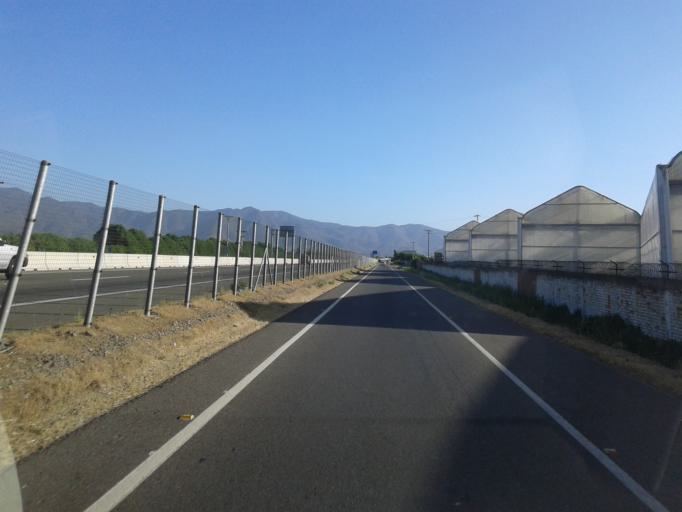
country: CL
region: Valparaiso
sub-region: Provincia de Quillota
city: Quillota
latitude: -32.8515
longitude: -71.2245
